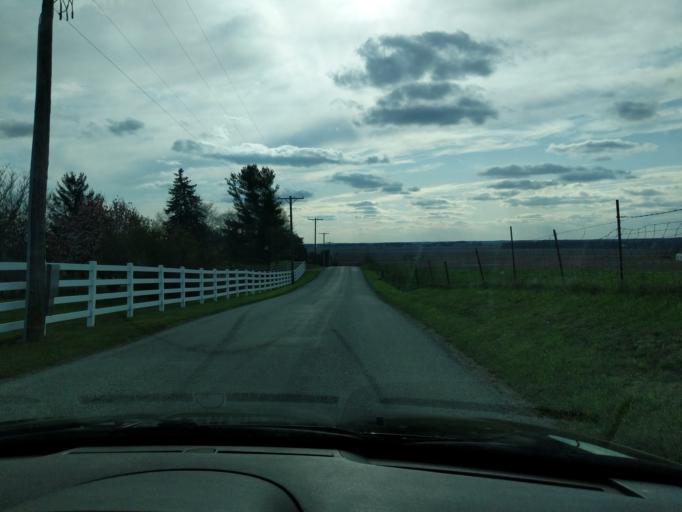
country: US
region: Ohio
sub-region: Champaign County
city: Urbana
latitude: 40.1290
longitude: -83.6697
